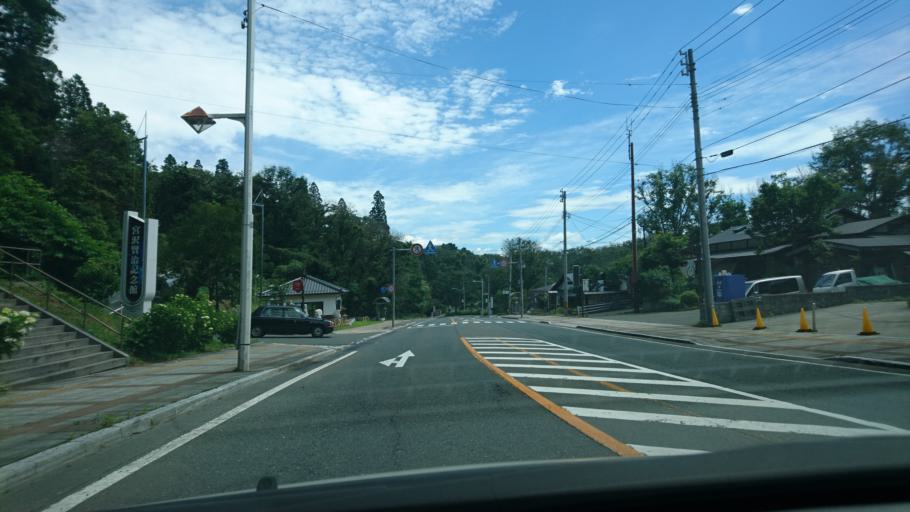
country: JP
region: Iwate
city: Hanamaki
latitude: 39.3984
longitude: 141.1656
